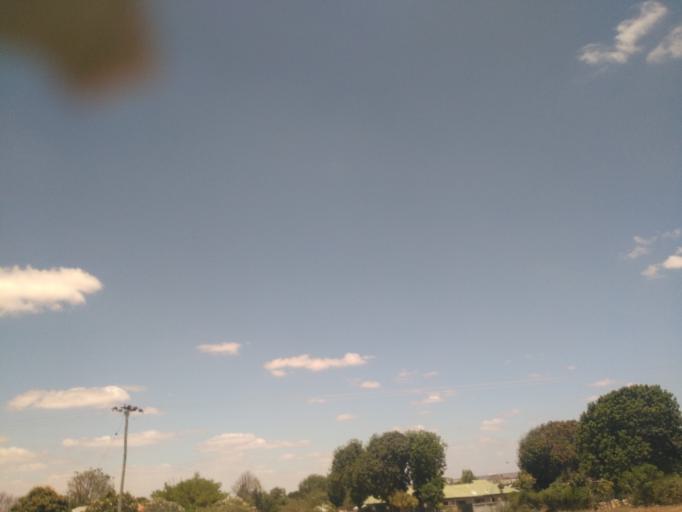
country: TZ
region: Dodoma
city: Dodoma
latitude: -6.1823
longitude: 35.7326
